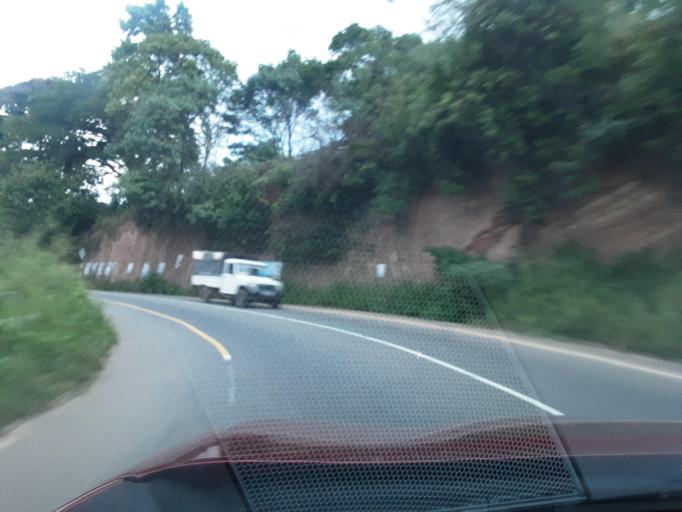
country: LK
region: Central
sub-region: Nuwara Eliya District
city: Nuwara Eliya
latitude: 6.9021
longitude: 80.9015
